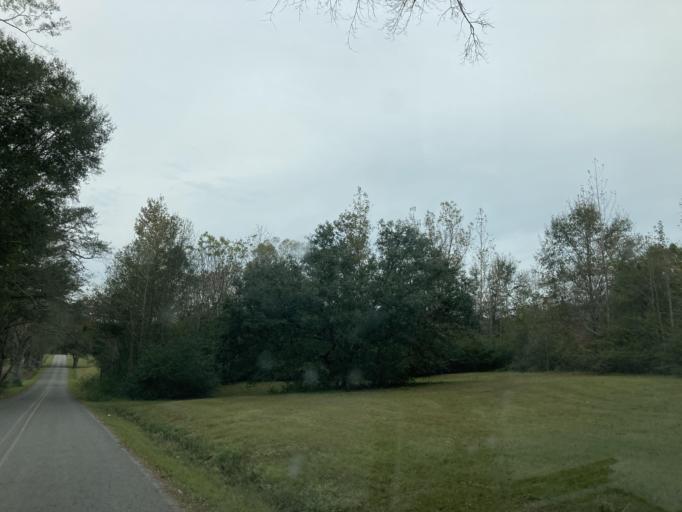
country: US
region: Mississippi
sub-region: Lamar County
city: Lumberton
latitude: 31.0504
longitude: -89.4508
